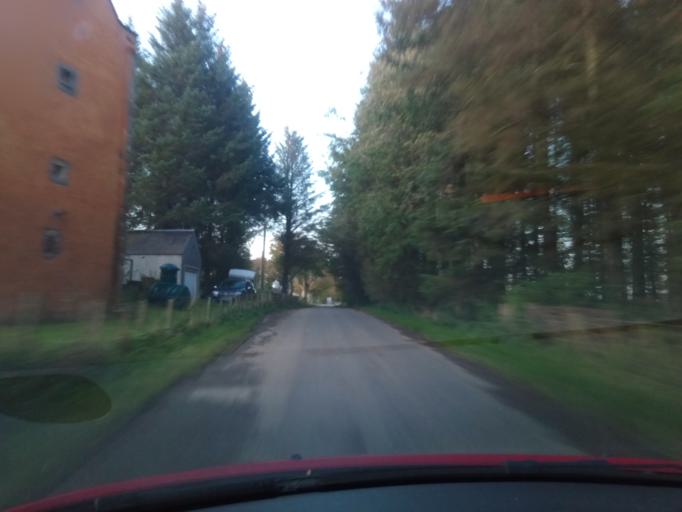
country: GB
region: Scotland
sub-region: East Lothian
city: Pencaitland
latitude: 55.7966
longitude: -2.8889
